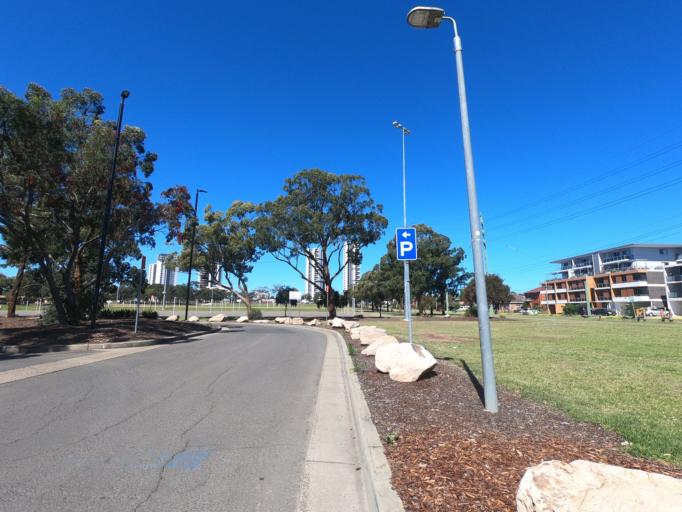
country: AU
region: New South Wales
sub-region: Liverpool
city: Miller
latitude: -33.9278
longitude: 150.9128
